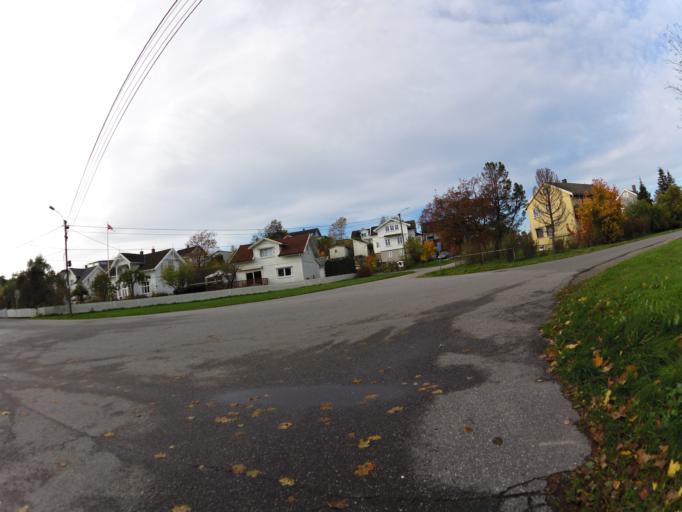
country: NO
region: Ostfold
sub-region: Fredrikstad
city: Fredrikstad
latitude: 59.2183
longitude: 10.9115
